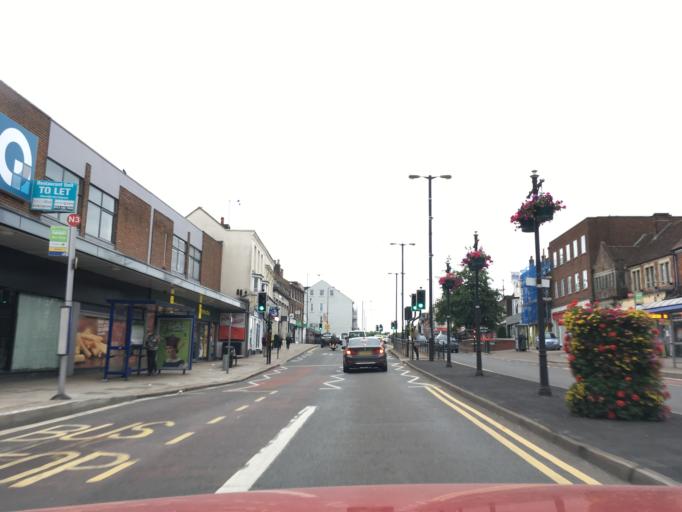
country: GB
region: England
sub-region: Central Bedfordshire
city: Dunstable
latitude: 51.8868
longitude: -0.5220
